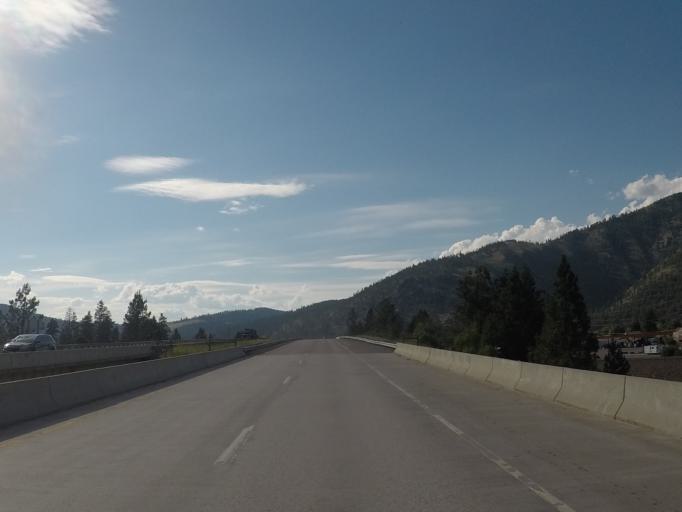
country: US
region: Montana
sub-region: Missoula County
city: Bonner-West Riverside
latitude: 46.8718
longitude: -113.8869
